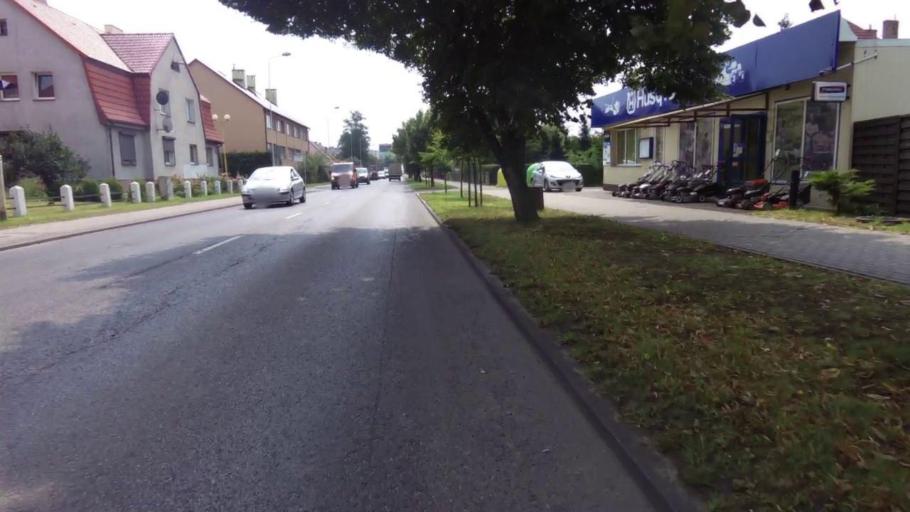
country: PL
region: West Pomeranian Voivodeship
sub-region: Powiat choszczenski
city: Choszczno
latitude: 53.1729
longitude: 15.4172
